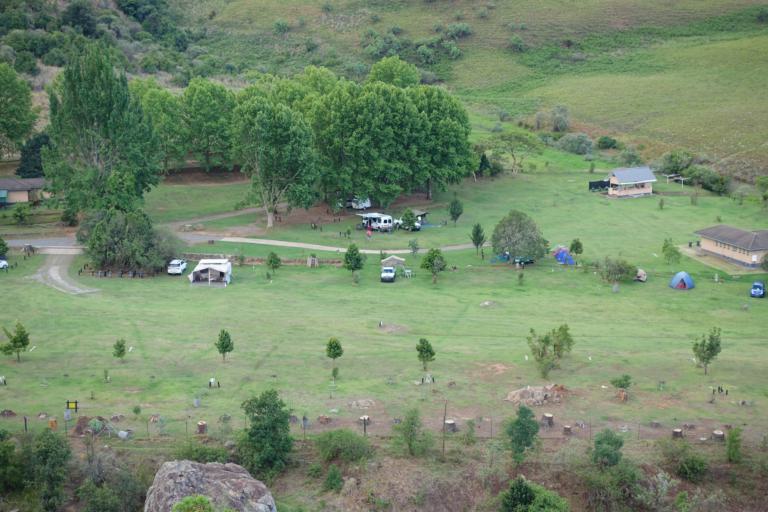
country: ZA
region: Orange Free State
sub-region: Thabo Mofutsanyana District Municipality
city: Phuthaditjhaba
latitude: -28.6913
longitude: 28.9473
